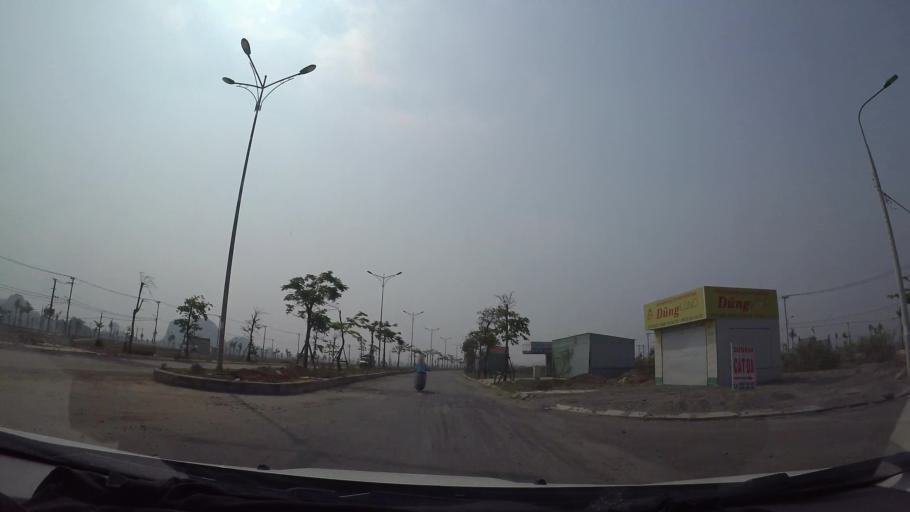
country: VN
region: Da Nang
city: Ngu Hanh Son
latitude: 16.0065
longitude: 108.2453
